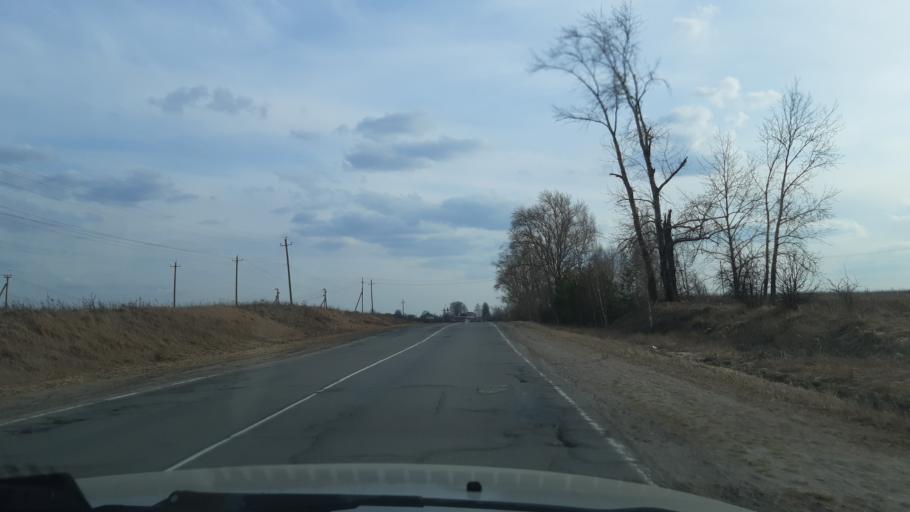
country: RU
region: Vladimir
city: Nikologory
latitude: 56.1567
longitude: 41.9959
